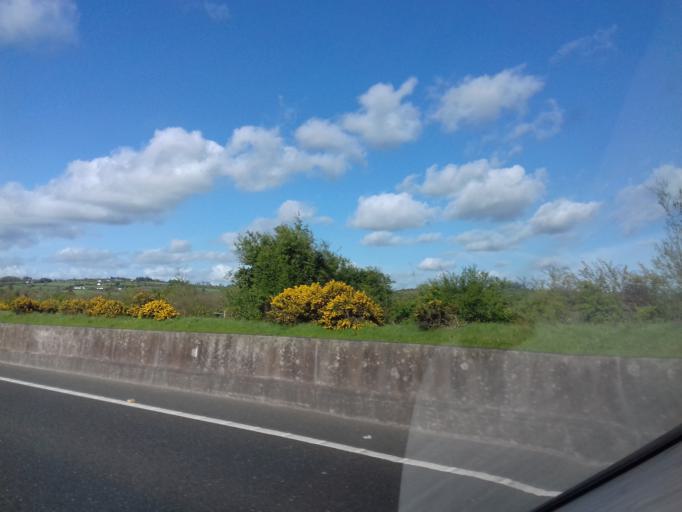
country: IE
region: Leinster
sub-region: Kilkenny
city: Mooncoin
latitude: 52.3567
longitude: -7.1666
